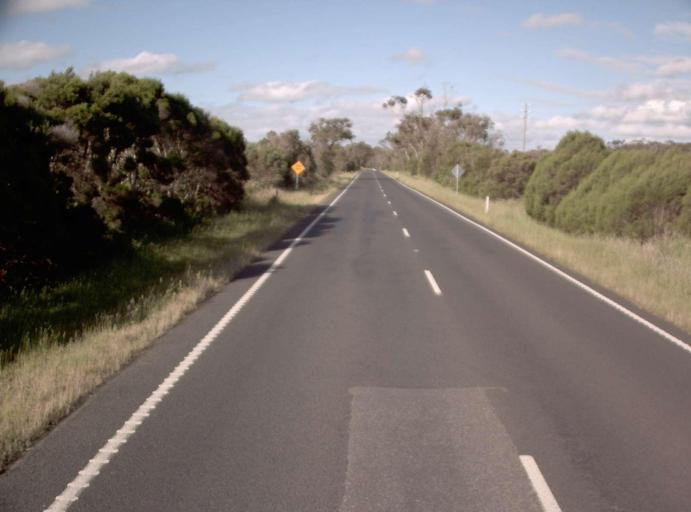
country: AU
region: Victoria
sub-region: Bass Coast
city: North Wonthaggi
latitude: -38.5746
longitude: 145.8336
